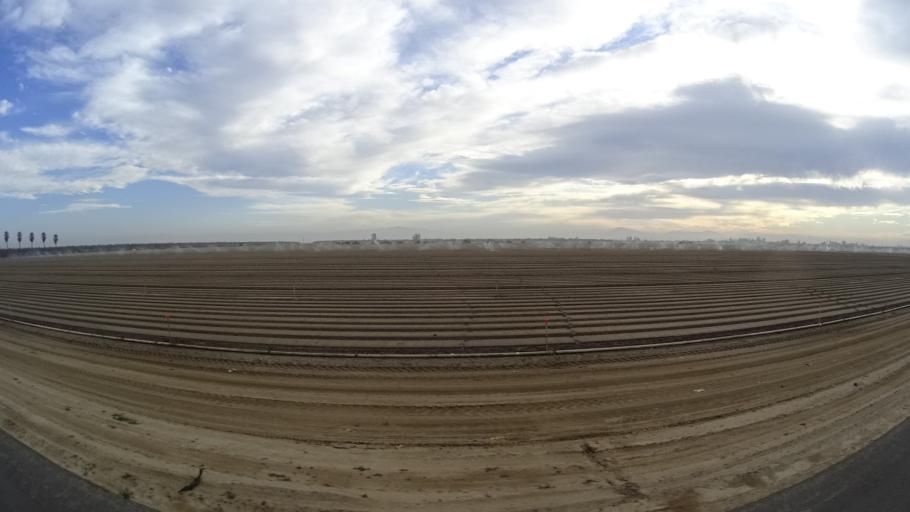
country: US
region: California
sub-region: Kern County
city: Rosedale
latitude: 35.4027
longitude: -119.1987
